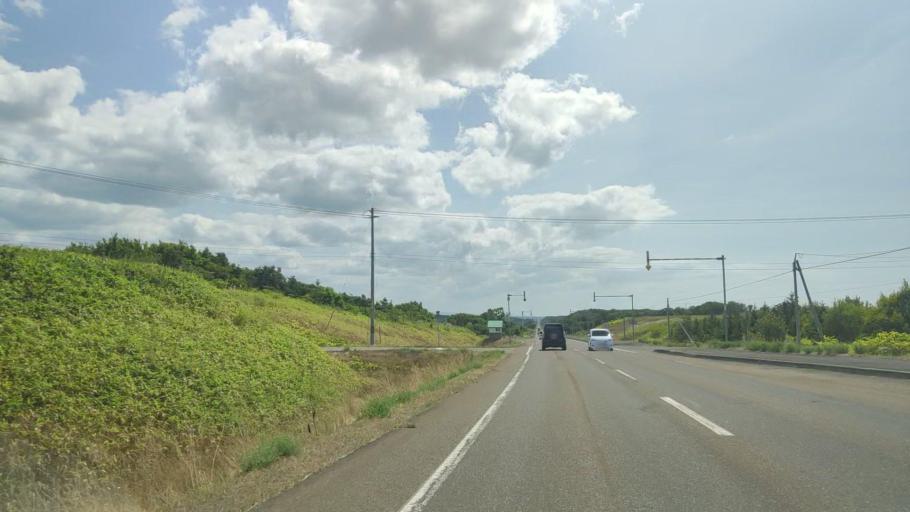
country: JP
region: Hokkaido
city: Makubetsu
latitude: 44.7857
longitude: 141.7902
